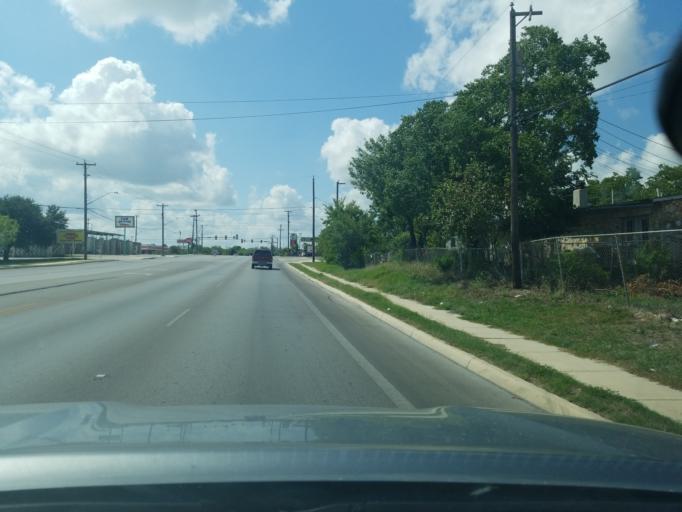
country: US
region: Texas
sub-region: Bexar County
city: Lackland Air Force Base
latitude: 29.3319
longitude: -98.5337
